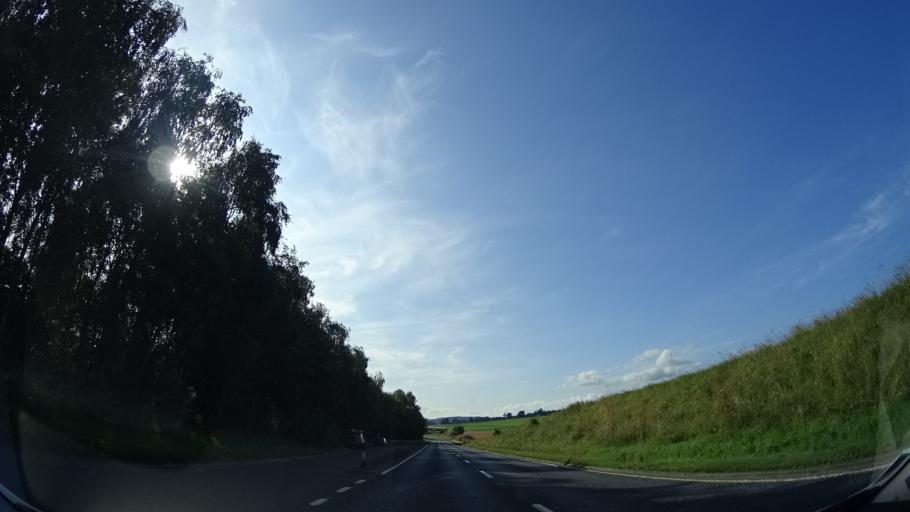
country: GB
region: Scotland
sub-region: Highland
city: Muir of Ord
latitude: 57.5594
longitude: -4.5490
